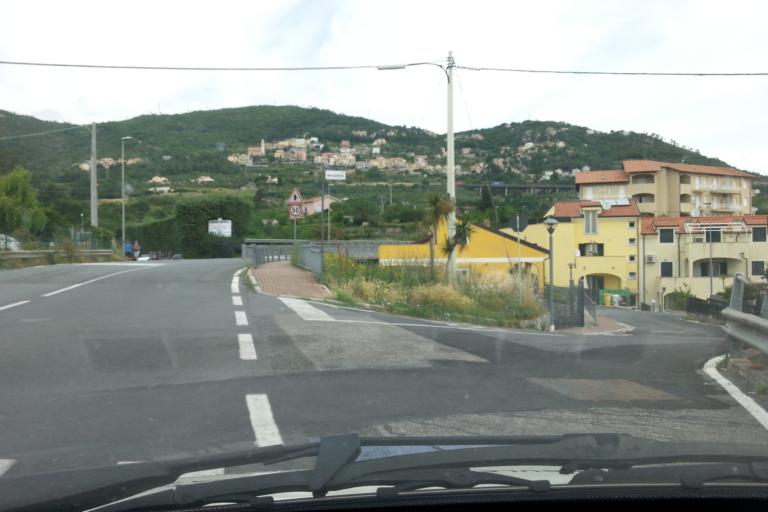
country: IT
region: Liguria
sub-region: Provincia di Savona
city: Pietra Ligure
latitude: 44.1470
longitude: 8.2693
